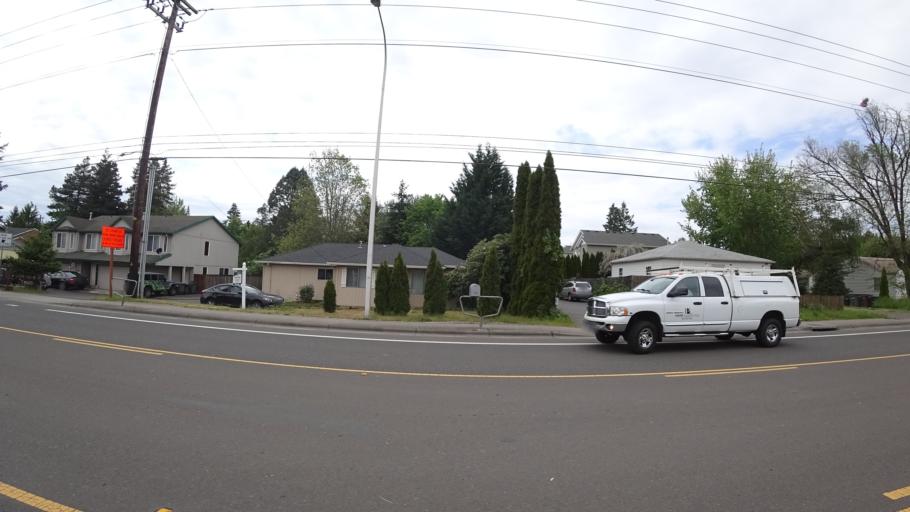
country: US
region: Oregon
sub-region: Washington County
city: Hillsboro
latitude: 45.5167
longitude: -122.9366
